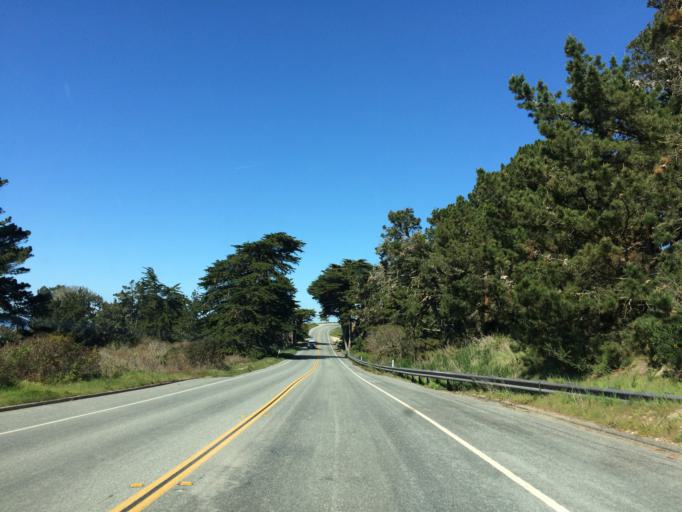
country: US
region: California
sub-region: Santa Cruz County
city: Bonny Doon
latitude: 37.0854
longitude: -122.2693
